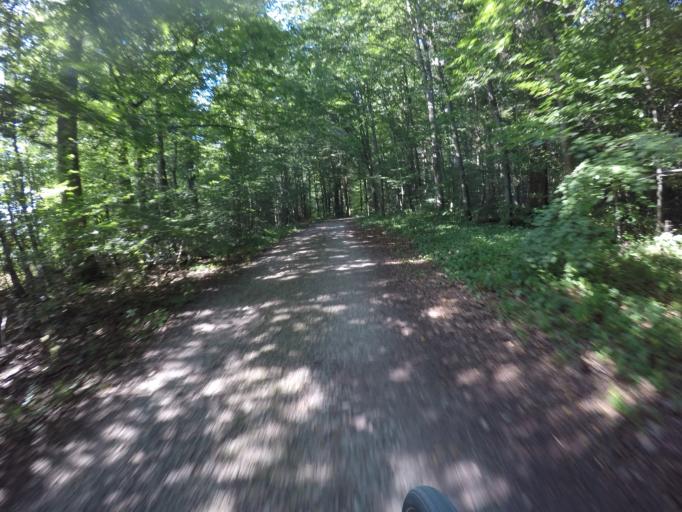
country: DE
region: Baden-Wuerttemberg
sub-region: Regierungsbezirk Stuttgart
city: Altdorf
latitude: 48.6568
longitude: 8.9833
